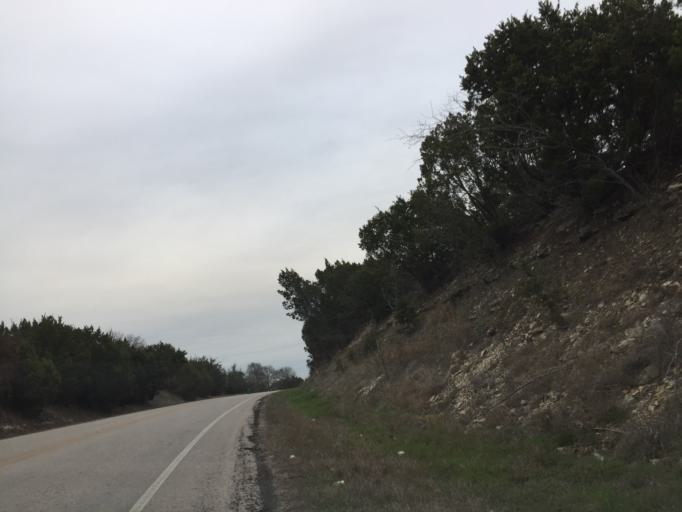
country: US
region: Texas
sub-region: Coryell County
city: Ames
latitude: 31.5061
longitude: -97.7269
